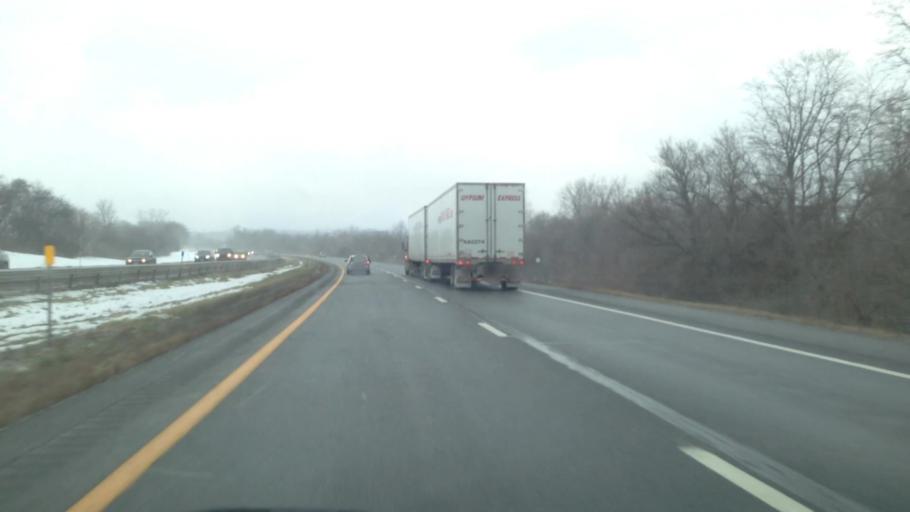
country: US
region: New York
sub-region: Montgomery County
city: Amsterdam
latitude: 42.9079
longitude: -74.1367
